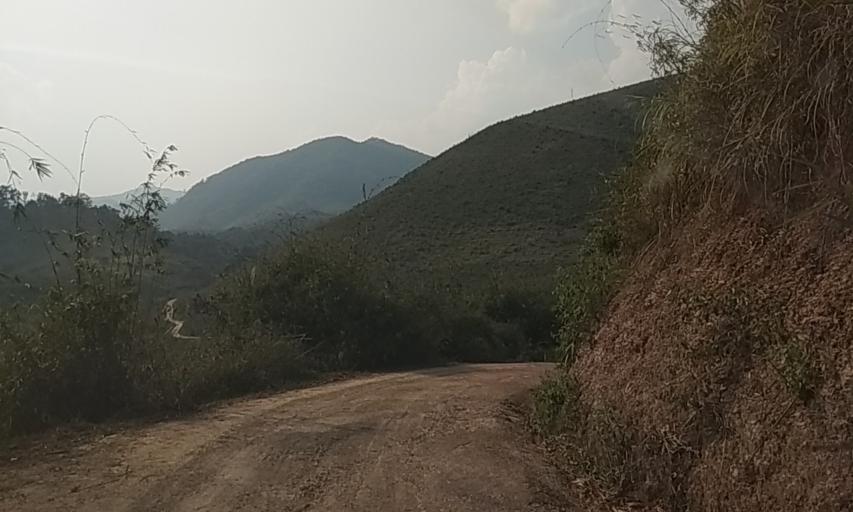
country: LA
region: Louangphabang
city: Louangphabang
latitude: 20.0408
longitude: 101.8124
